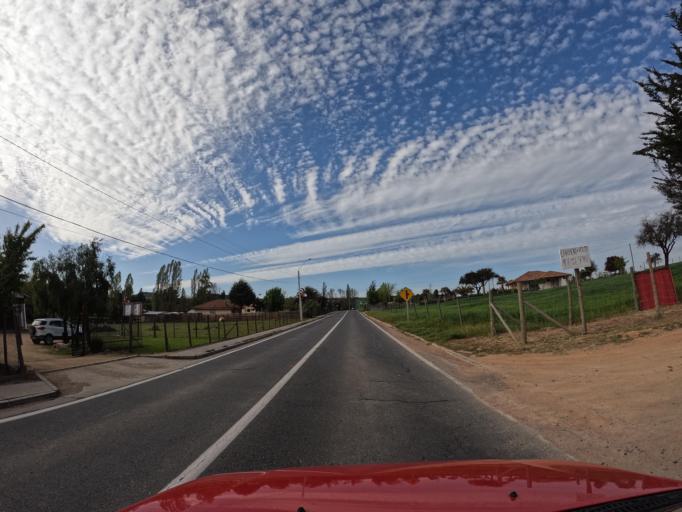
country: CL
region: O'Higgins
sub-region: Provincia de Colchagua
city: Santa Cruz
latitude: -34.2203
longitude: -71.7208
